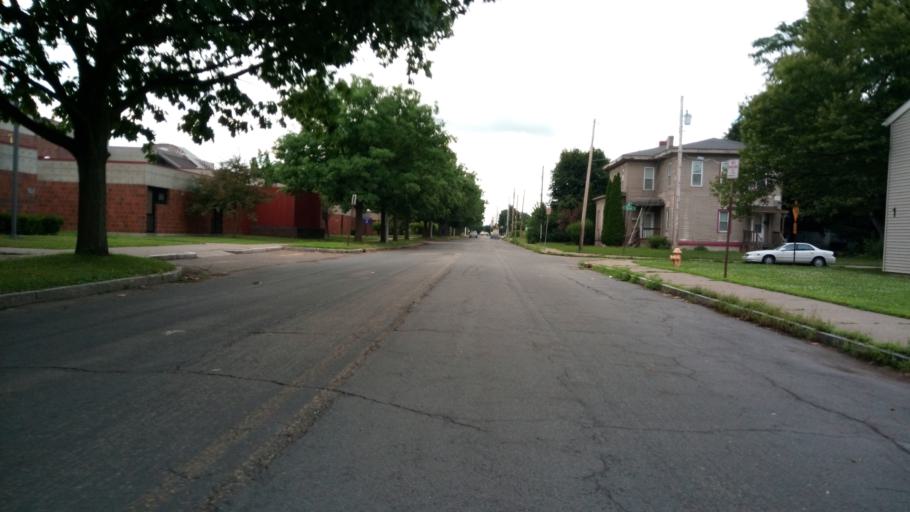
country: US
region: New York
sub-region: Chemung County
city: Elmira
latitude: 42.0922
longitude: -76.7929
